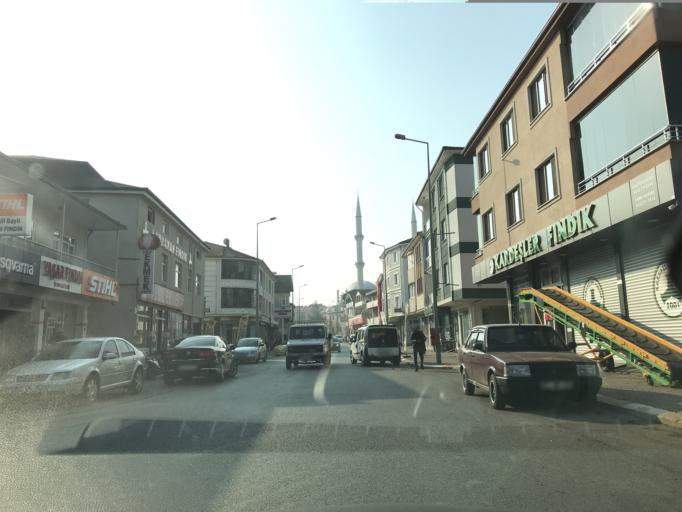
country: TR
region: Duzce
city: Cumayeri
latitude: 40.8784
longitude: 30.9504
